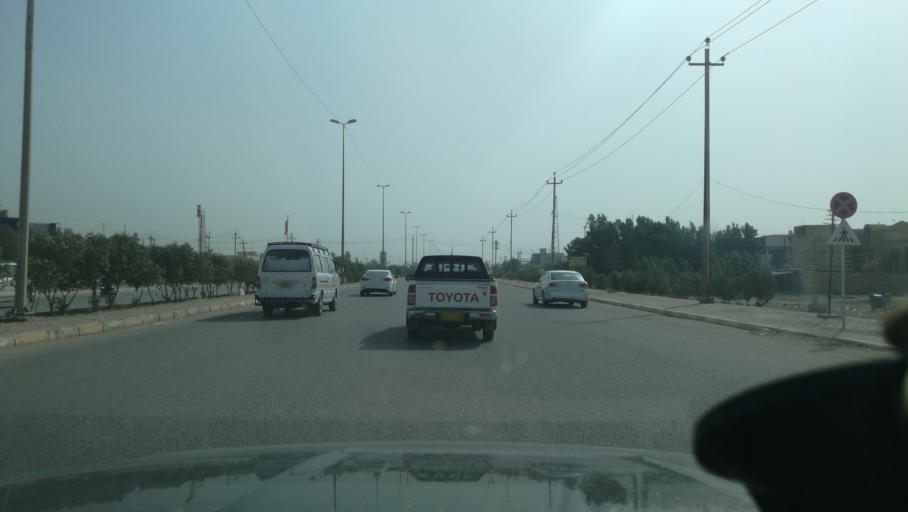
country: IQ
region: Dhi Qar
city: An Nasiriyah
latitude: 31.0648
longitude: 46.2483
